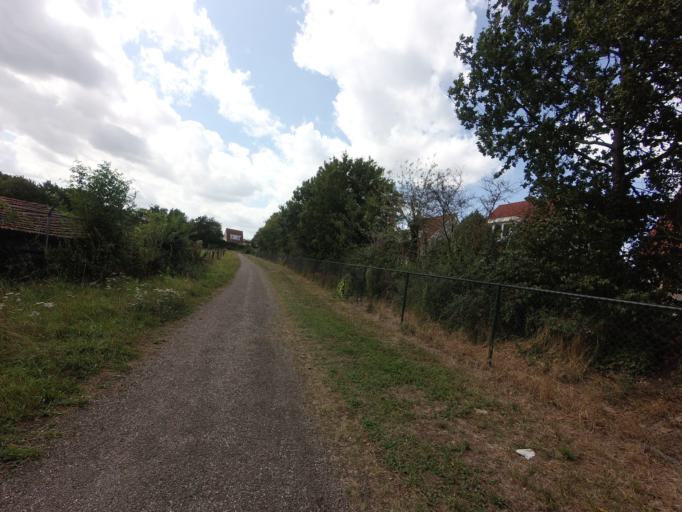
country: NL
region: Limburg
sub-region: Gemeente Maasgouw
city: Maasbracht
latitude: 51.1336
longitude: 5.8579
